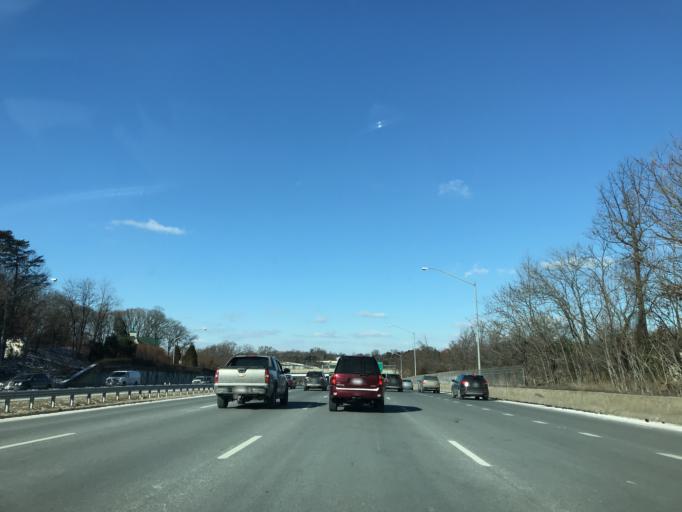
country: US
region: Maryland
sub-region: Prince George's County
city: Camp Springs
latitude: 38.8144
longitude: -76.9133
